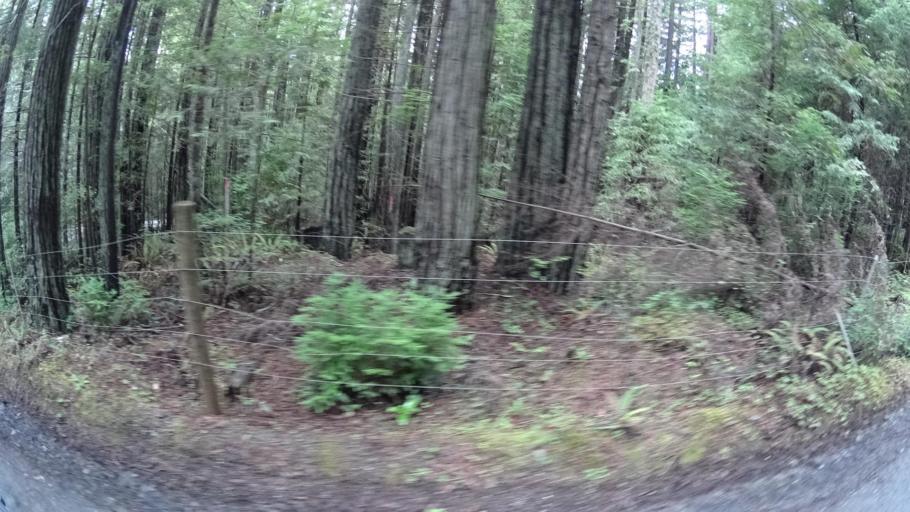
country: US
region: California
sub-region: Humboldt County
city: Blue Lake
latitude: 40.9050
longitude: -123.9753
